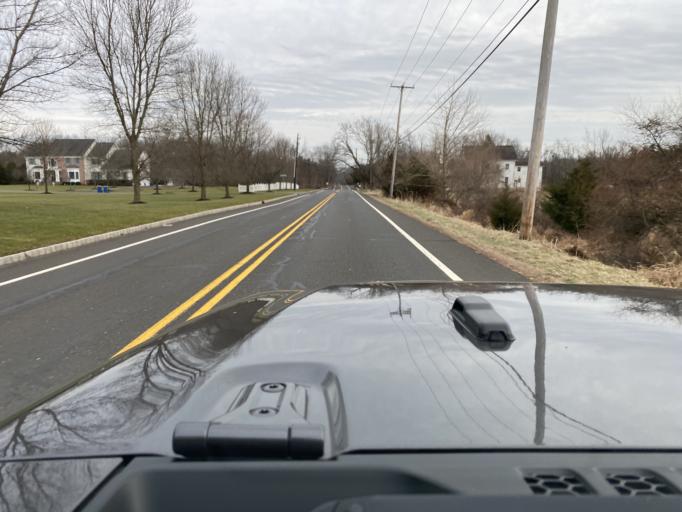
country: US
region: New Jersey
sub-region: Hunterdon County
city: Whitehouse Station
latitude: 40.5345
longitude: -74.7489
